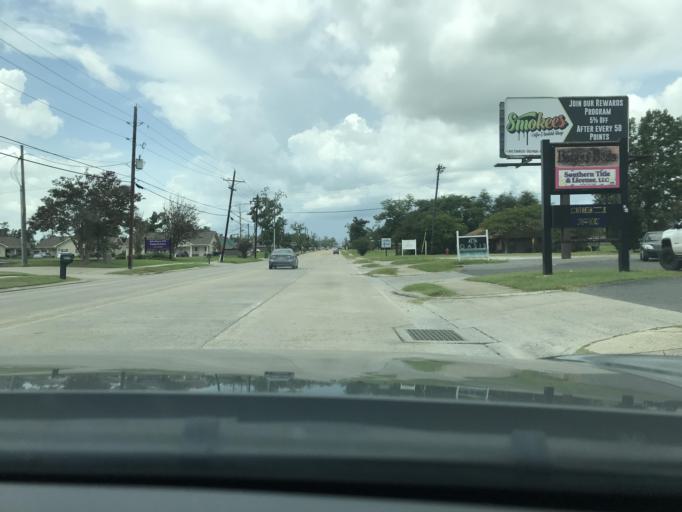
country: US
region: Louisiana
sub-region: Calcasieu Parish
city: Sulphur
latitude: 30.2277
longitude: -93.3280
